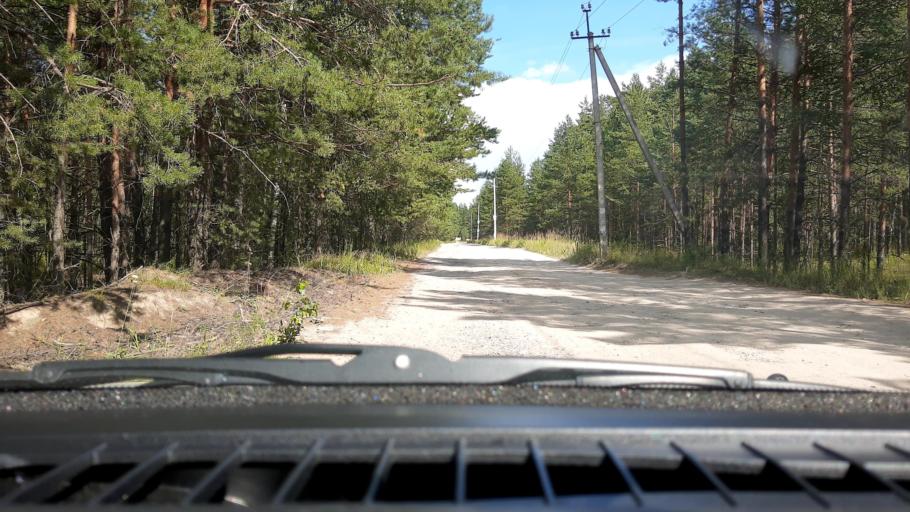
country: RU
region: Nizjnij Novgorod
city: Babino
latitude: 56.3331
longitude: 43.6447
